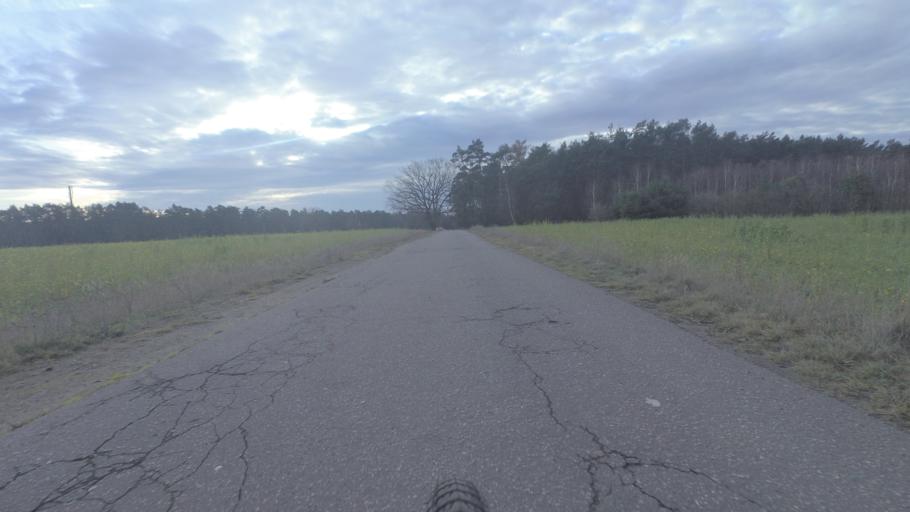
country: DE
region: Brandenburg
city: Am Mellensee
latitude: 52.2329
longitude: 13.3584
